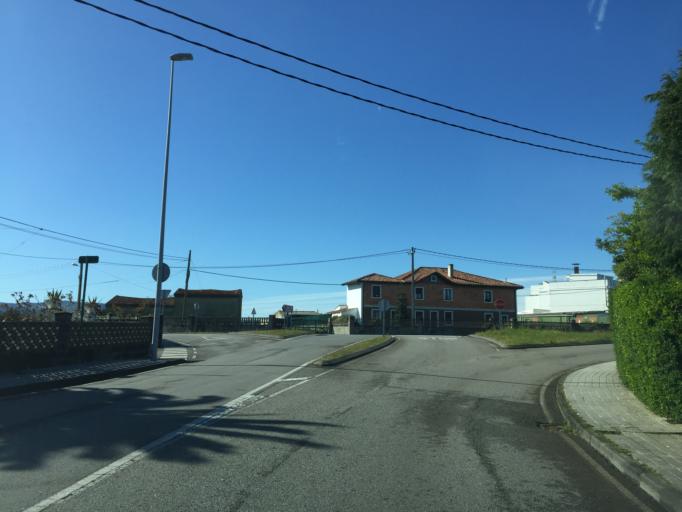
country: ES
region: Asturias
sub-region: Province of Asturias
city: Gijon
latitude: 43.5495
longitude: -5.6160
